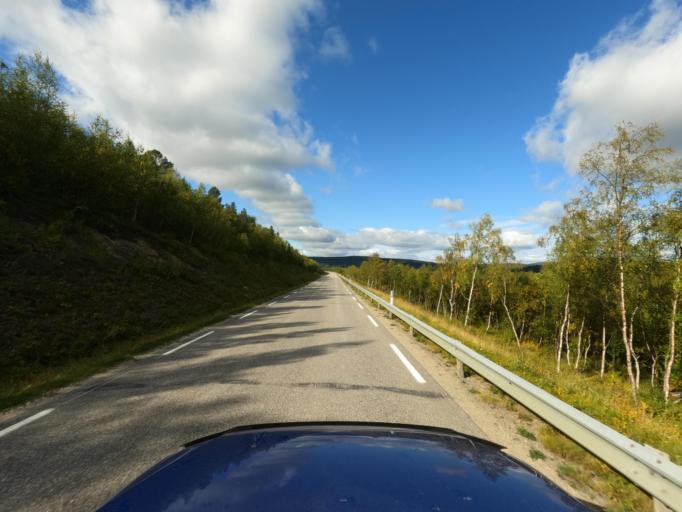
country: NO
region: Finnmark Fylke
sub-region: Karasjok
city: Karasjohka
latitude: 69.4552
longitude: 25.5684
